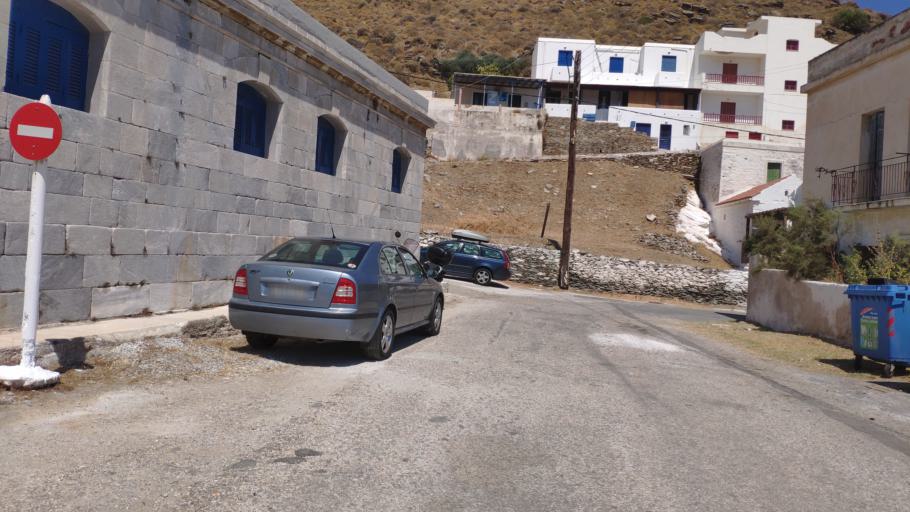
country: GR
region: South Aegean
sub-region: Nomos Kykladon
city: Kythnos
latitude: 37.4410
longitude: 24.4246
